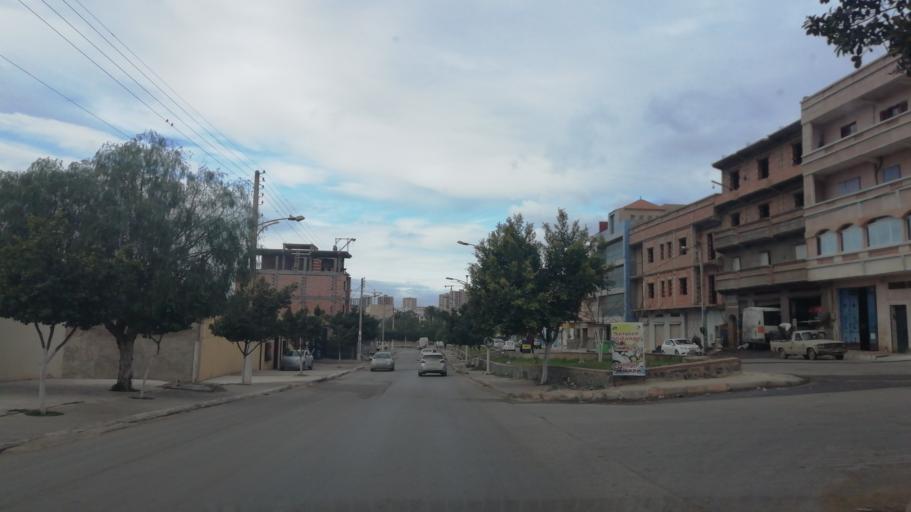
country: DZ
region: Oran
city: Bir el Djir
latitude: 35.7213
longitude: -0.5624
